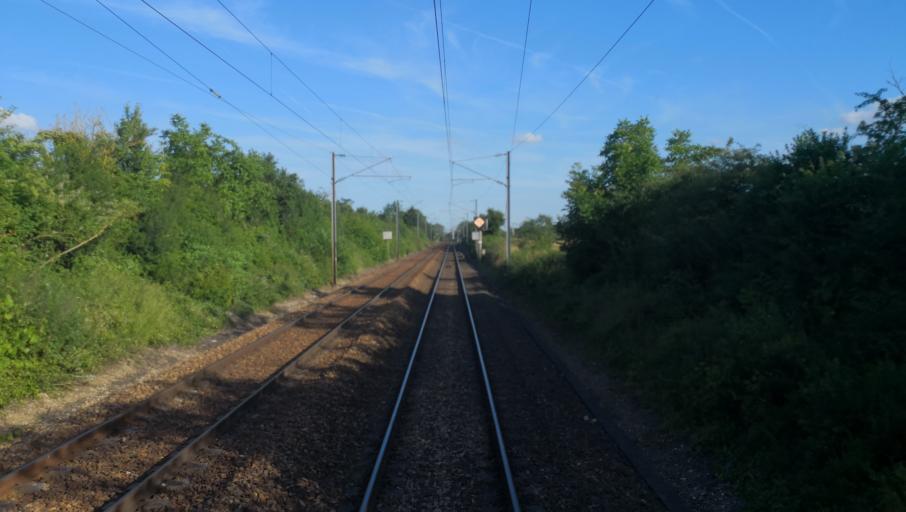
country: FR
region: Haute-Normandie
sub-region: Departement de l'Eure
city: Bueil
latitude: 48.9340
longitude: 1.4363
